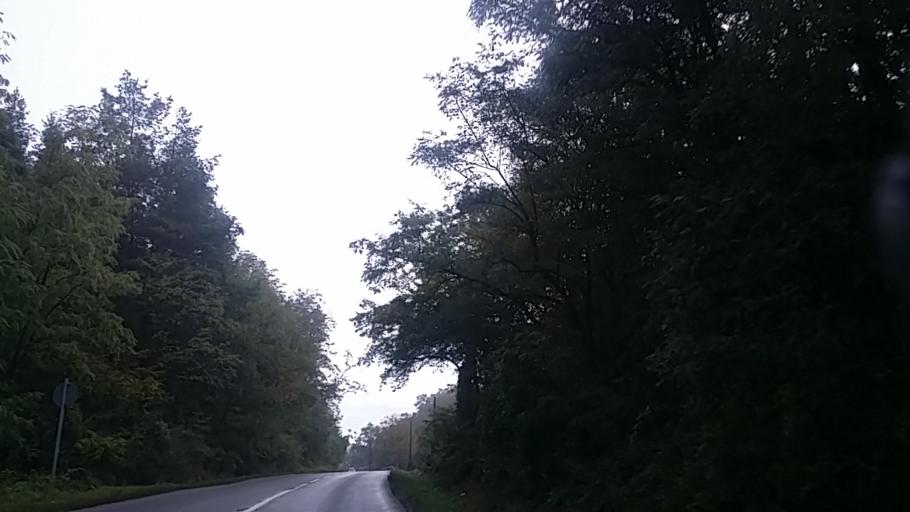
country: HU
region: Heves
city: Szilvasvarad
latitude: 48.0883
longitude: 20.3738
